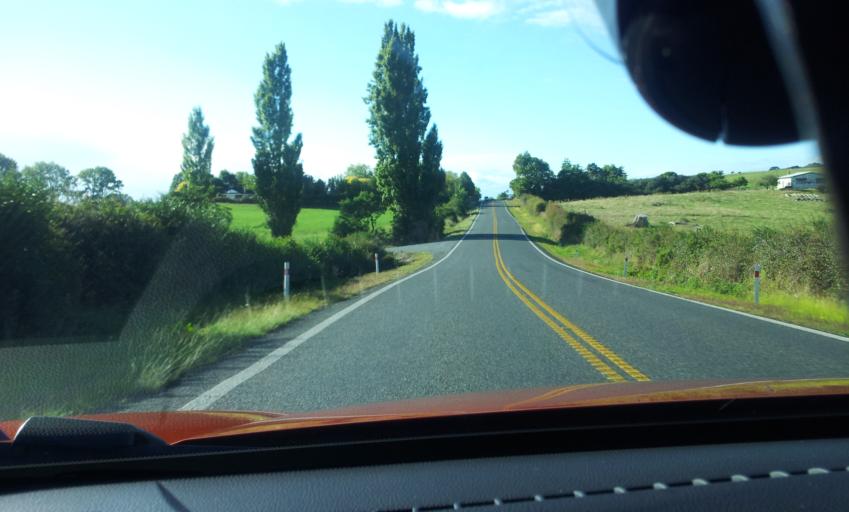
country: NZ
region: Waikato
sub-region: Hauraki District
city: Ngatea
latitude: -37.3768
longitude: 175.4289
